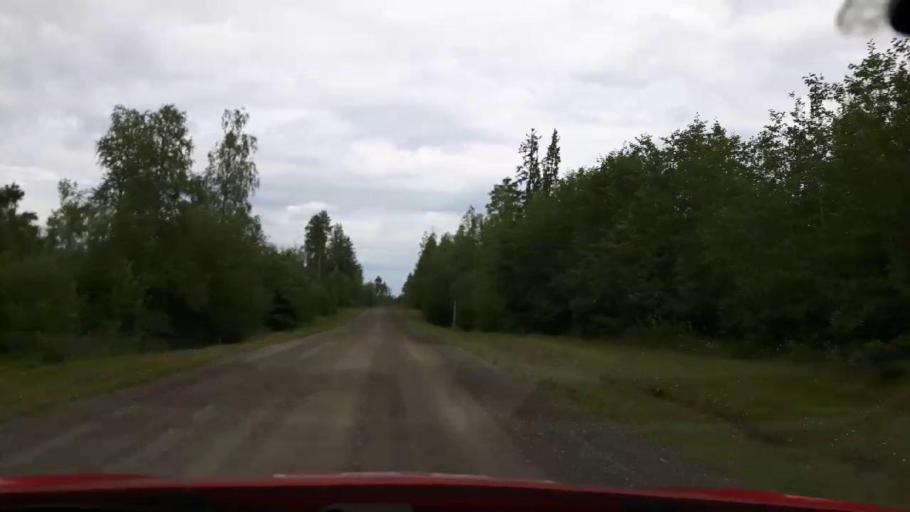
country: SE
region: Jaemtland
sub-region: Stroemsunds Kommun
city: Stroemsund
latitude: 63.7989
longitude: 15.6144
